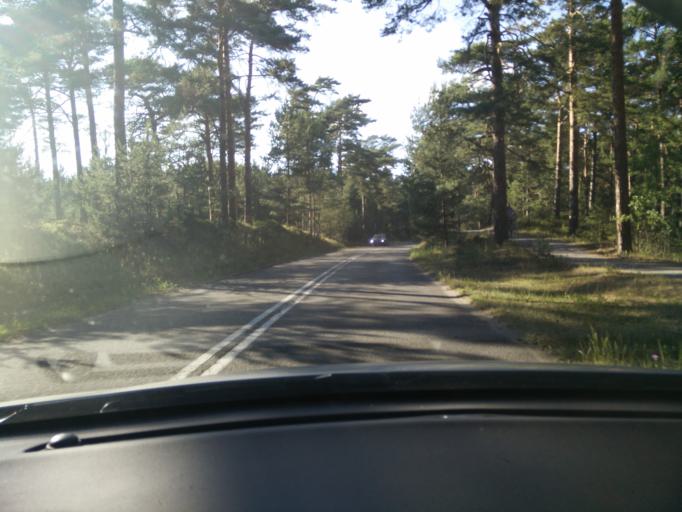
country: PL
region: Pomeranian Voivodeship
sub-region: Powiat pucki
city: Hel
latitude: 54.6439
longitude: 18.7709
